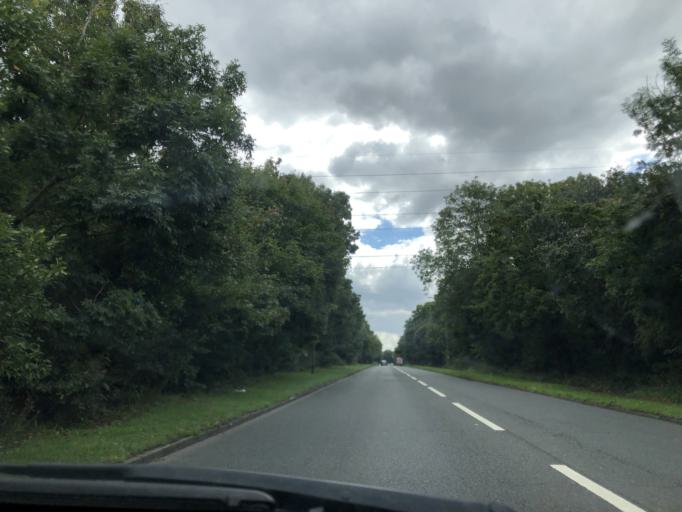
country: GB
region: England
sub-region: Kent
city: Halstead
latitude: 51.3530
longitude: 0.1282
